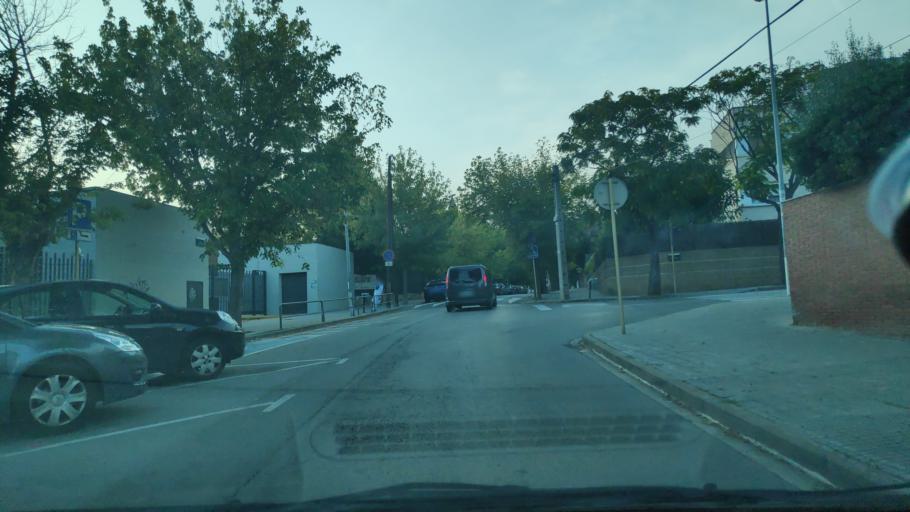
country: ES
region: Catalonia
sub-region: Provincia de Barcelona
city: Cerdanyola del Valles
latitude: 41.4869
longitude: 2.1356
